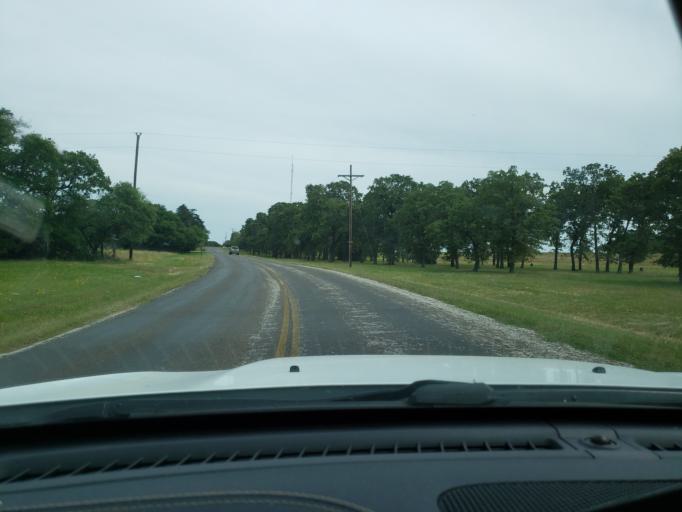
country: US
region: Texas
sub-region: Burleson County
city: Somerville
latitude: 30.3391
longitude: -96.5430
